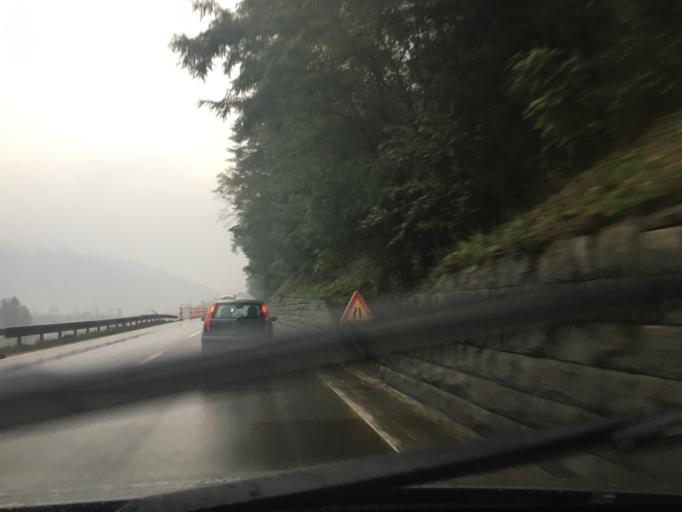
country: RS
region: Central Serbia
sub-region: Pcinjski Okrug
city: Vladicin Han
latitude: 42.7986
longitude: 22.1007
